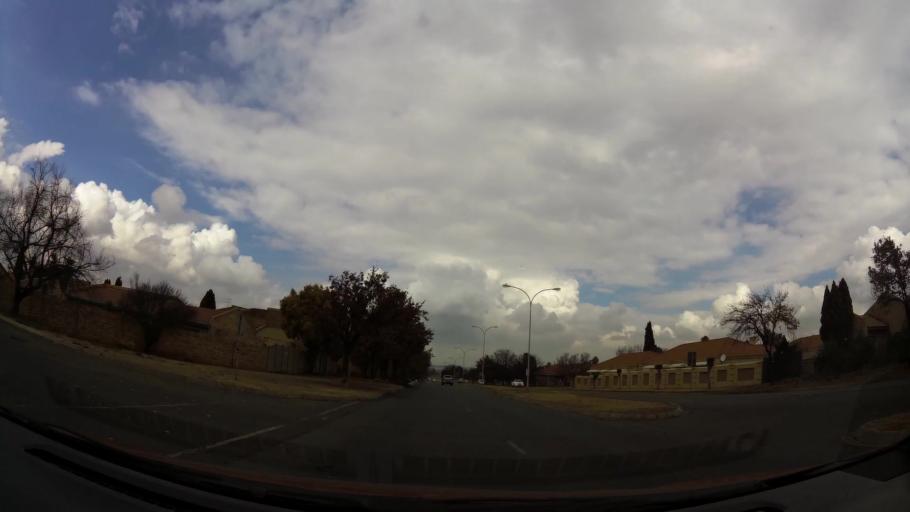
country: ZA
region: Gauteng
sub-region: Sedibeng District Municipality
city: Vanderbijlpark
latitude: -26.7319
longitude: 27.8539
